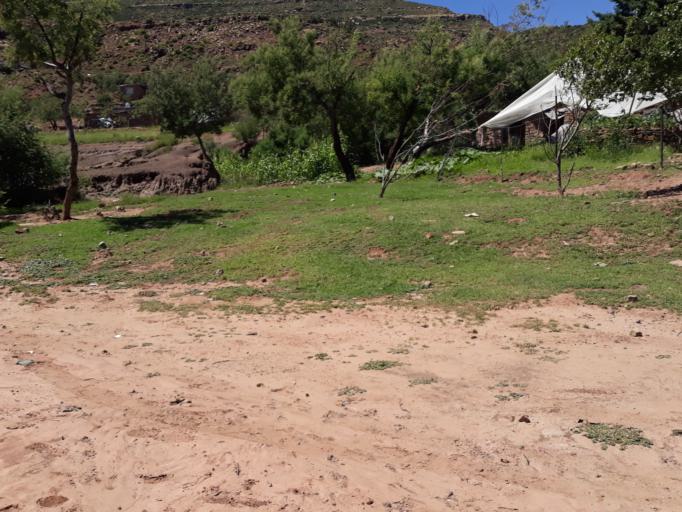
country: LS
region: Quthing
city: Quthing
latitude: -30.3403
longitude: 27.5400
